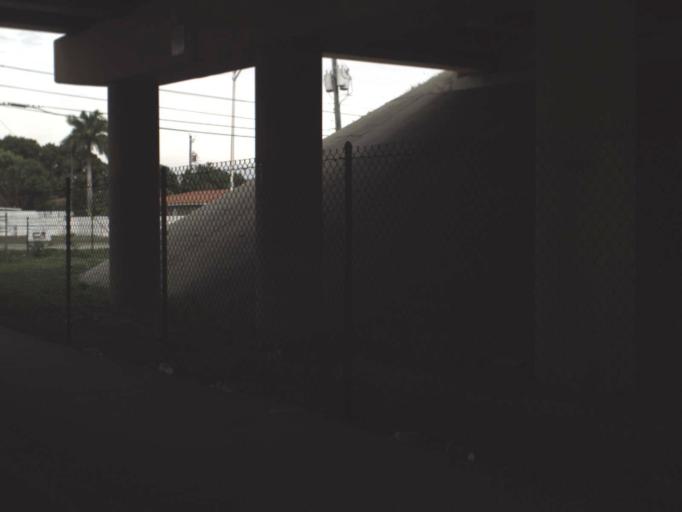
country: US
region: Florida
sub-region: Miami-Dade County
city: Brownsville
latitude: 25.7860
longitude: -80.2558
